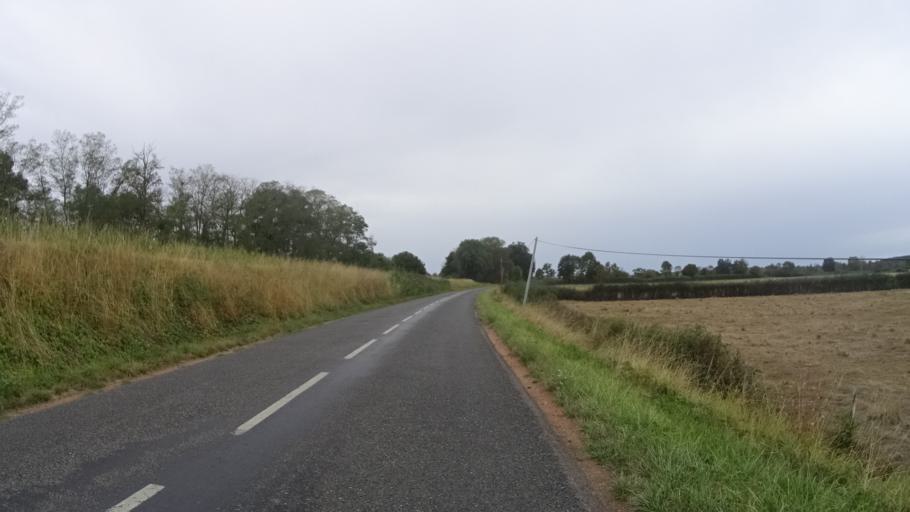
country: FR
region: Bourgogne
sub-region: Departement de la Nievre
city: Decize
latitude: 46.7900
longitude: 3.5140
